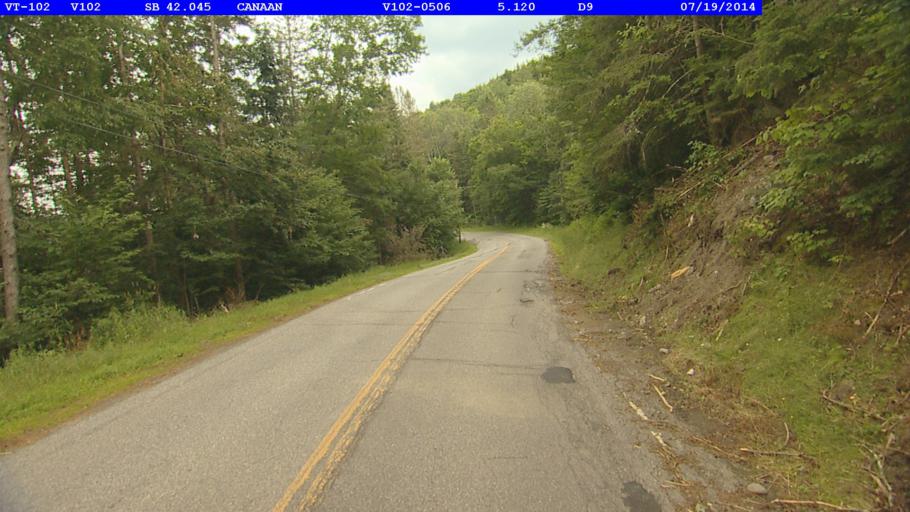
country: US
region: New Hampshire
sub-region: Coos County
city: Colebrook
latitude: 44.9744
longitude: -71.5357
